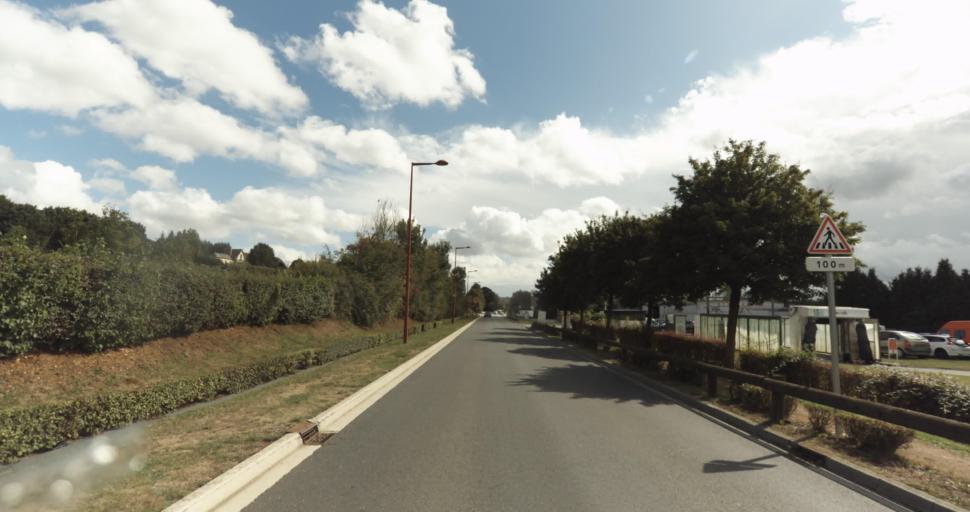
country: FR
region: Lower Normandy
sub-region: Departement de l'Orne
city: Gace
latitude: 48.7855
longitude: 0.2954
